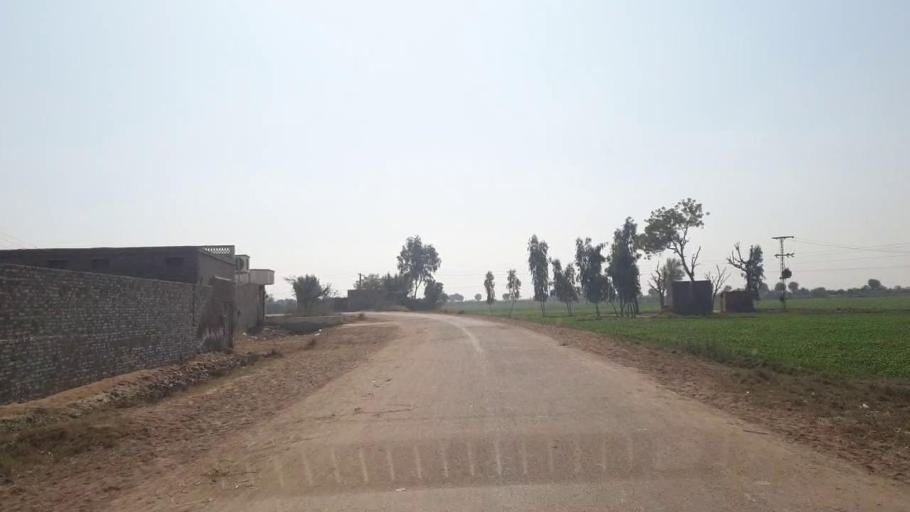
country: PK
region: Sindh
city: Sakrand
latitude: 26.0451
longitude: 68.4213
